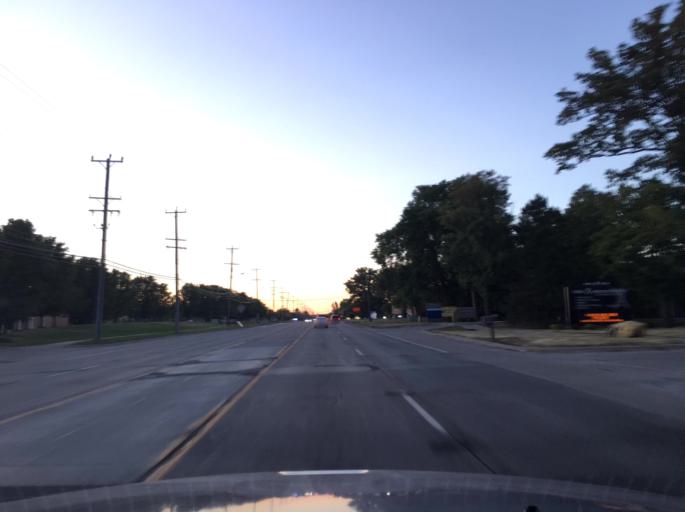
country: US
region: Michigan
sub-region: Macomb County
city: Clinton
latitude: 42.6183
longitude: -82.9531
